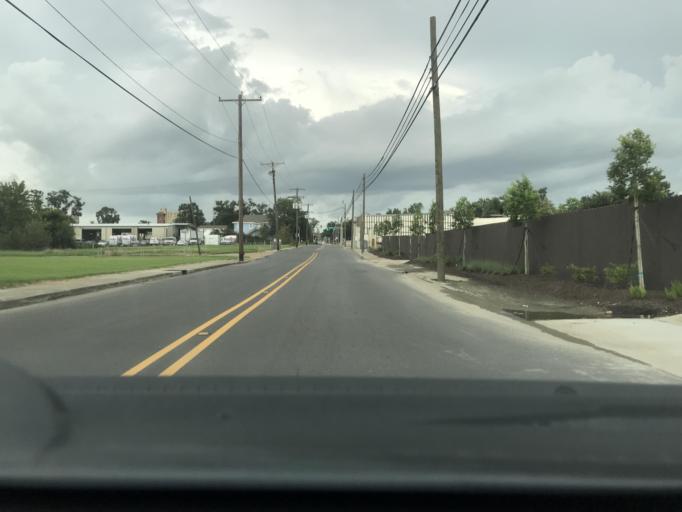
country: US
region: Louisiana
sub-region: Calcasieu Parish
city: Lake Charles
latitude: 30.2215
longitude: -93.2159
